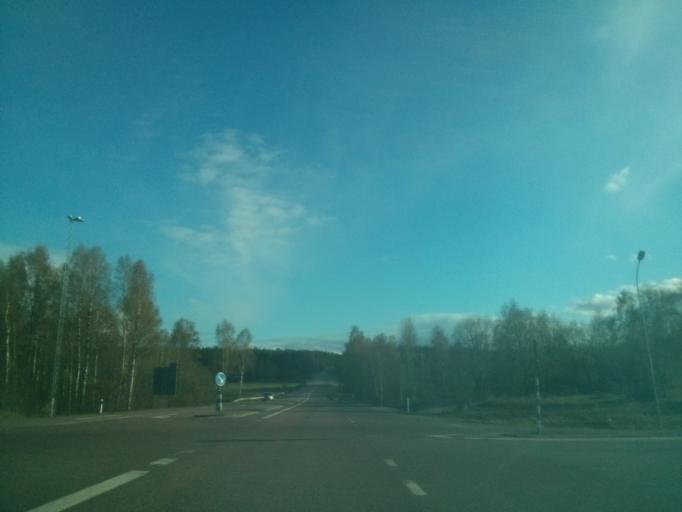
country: SE
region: Gaevleborg
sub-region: Nordanstigs Kommun
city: Bergsjoe
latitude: 62.0447
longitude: 17.2655
